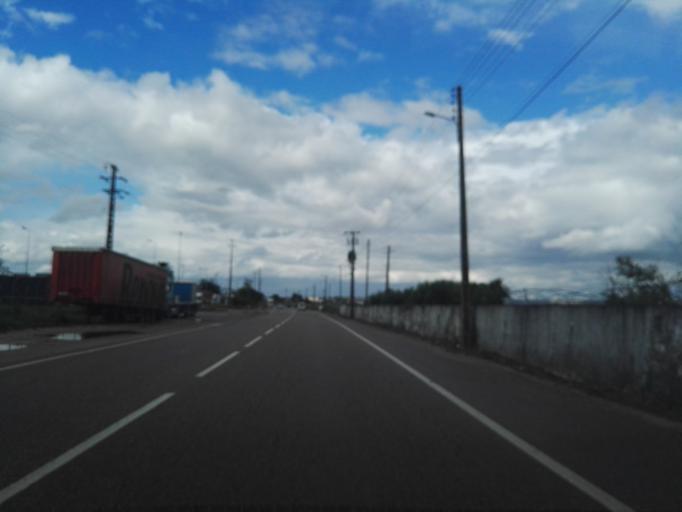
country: PT
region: Santarem
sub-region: Torres Novas
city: Riachos
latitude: 39.4342
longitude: -8.4984
